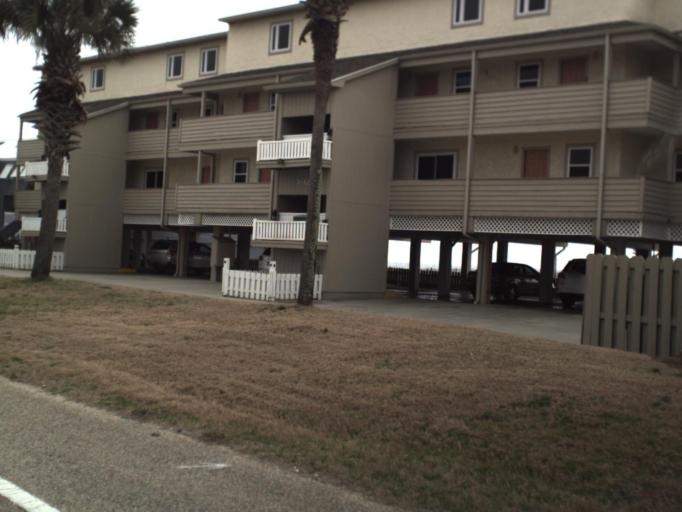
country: US
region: Florida
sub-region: Bay County
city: Laguna Beach
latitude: 30.2609
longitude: -85.9734
